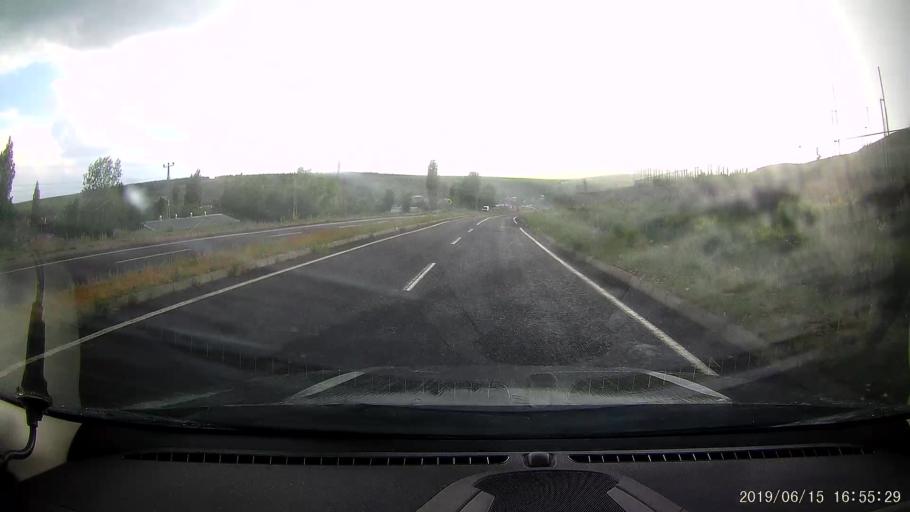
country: TR
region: Kars
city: Susuz
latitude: 40.7836
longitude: 43.1334
